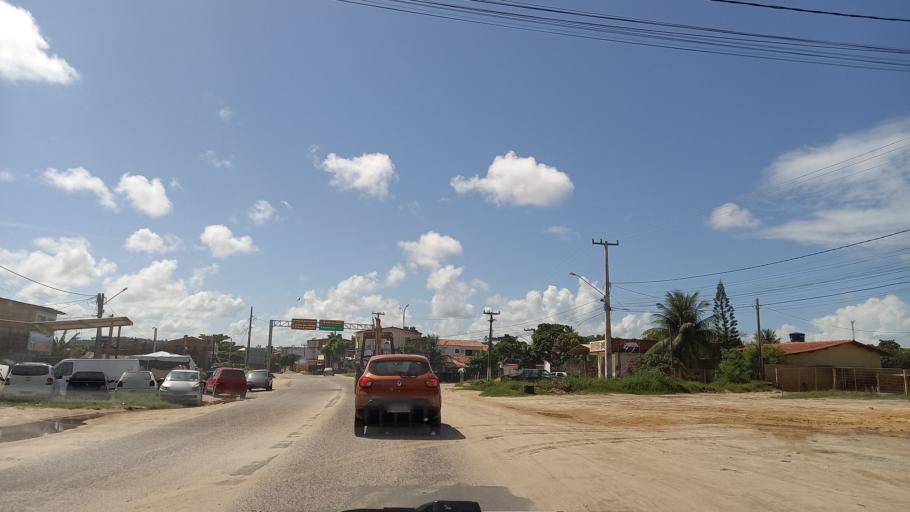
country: BR
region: Pernambuco
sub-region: Sao Jose Da Coroa Grande
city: Sao Jose da Coroa Grande
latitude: -8.8926
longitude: -35.1503
